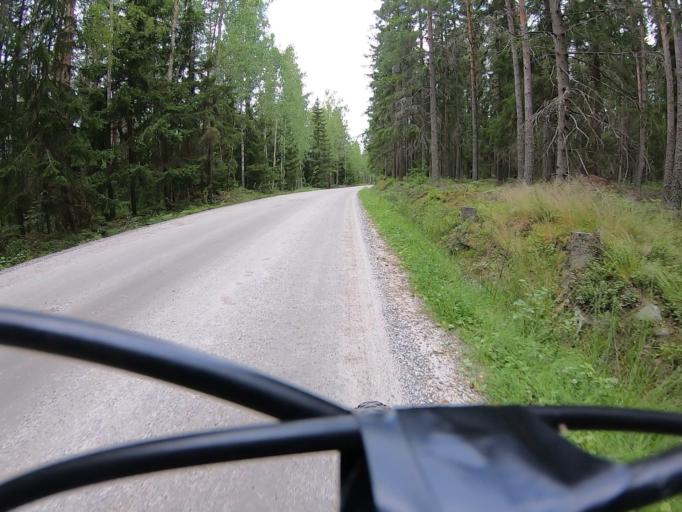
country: FI
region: Varsinais-Suomi
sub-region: Vakka-Suomi
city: Uusikaupunki
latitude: 60.8475
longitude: 21.3779
